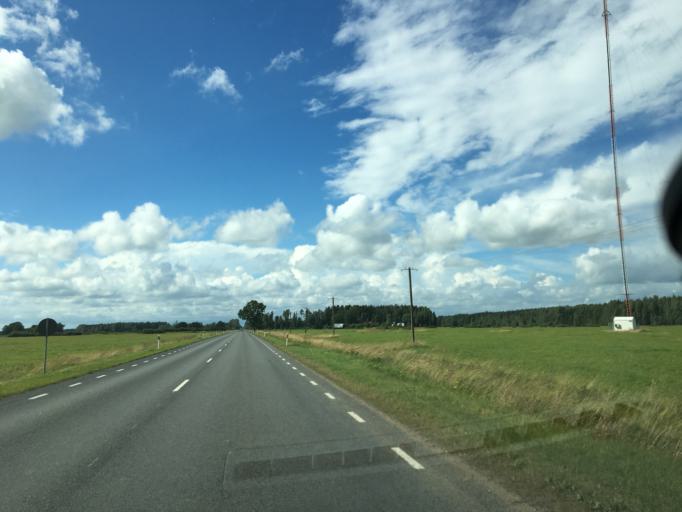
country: EE
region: Paernumaa
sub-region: Vaendra vald (alev)
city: Vandra
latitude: 58.5767
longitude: 25.1931
